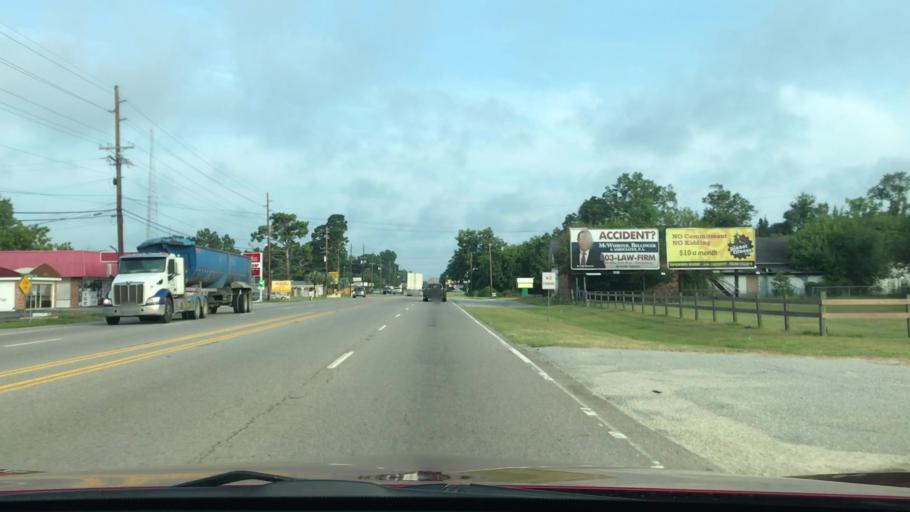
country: US
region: South Carolina
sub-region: Orangeburg County
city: Wilkinson Heights
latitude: 33.4765
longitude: -80.8151
